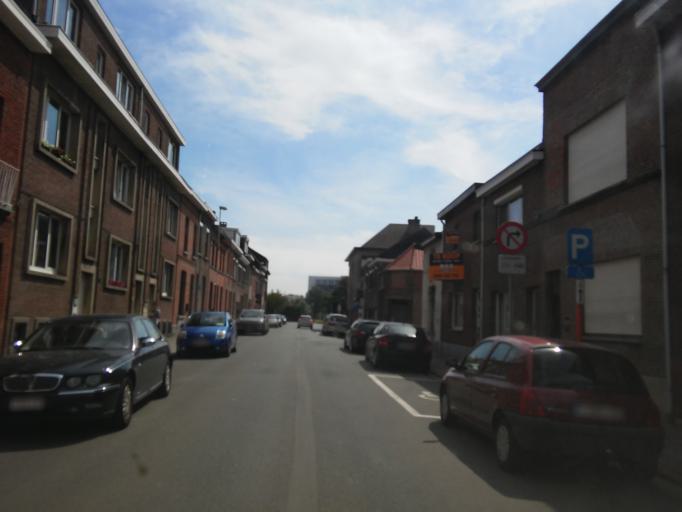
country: BE
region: Flanders
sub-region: Provincie Antwerpen
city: Boom
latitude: 51.0913
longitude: 4.3687
